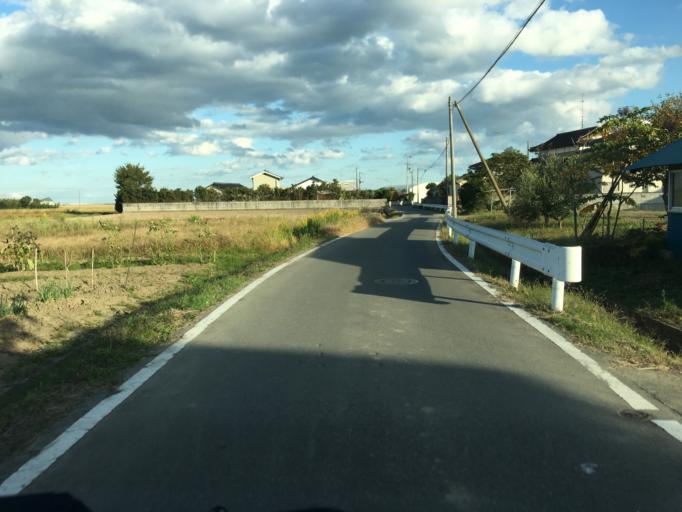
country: JP
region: Miyagi
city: Marumori
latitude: 37.7896
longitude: 140.9528
